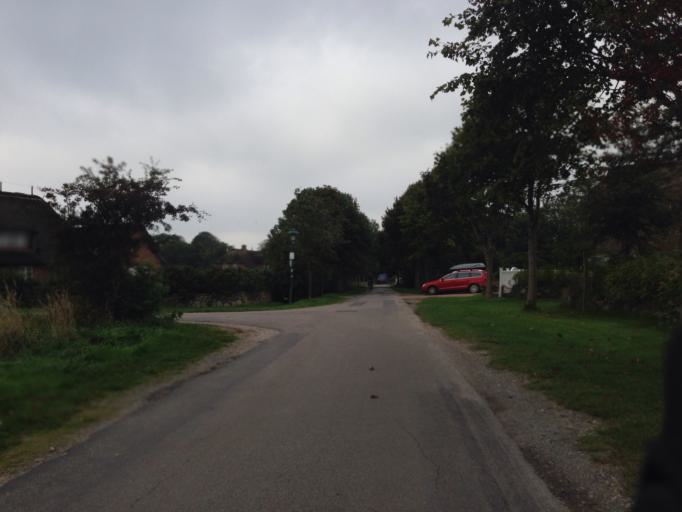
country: DE
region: Schleswig-Holstein
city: Nieblum
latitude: 54.6937
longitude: 8.4956
